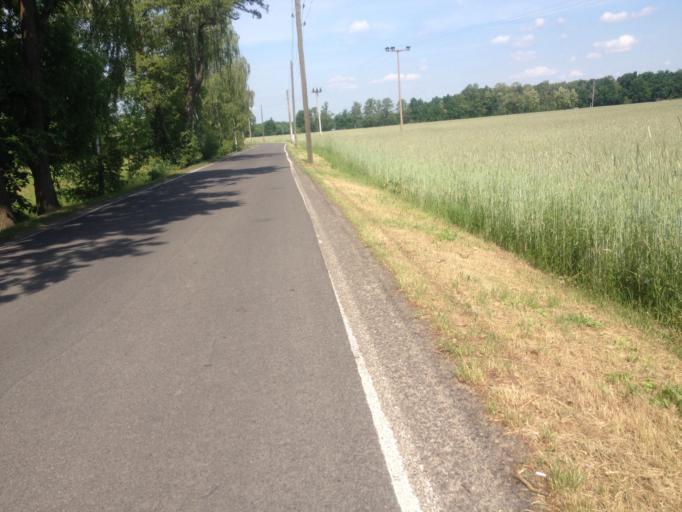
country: DE
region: Brandenburg
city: Cottbus
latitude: 51.8169
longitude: 14.3257
